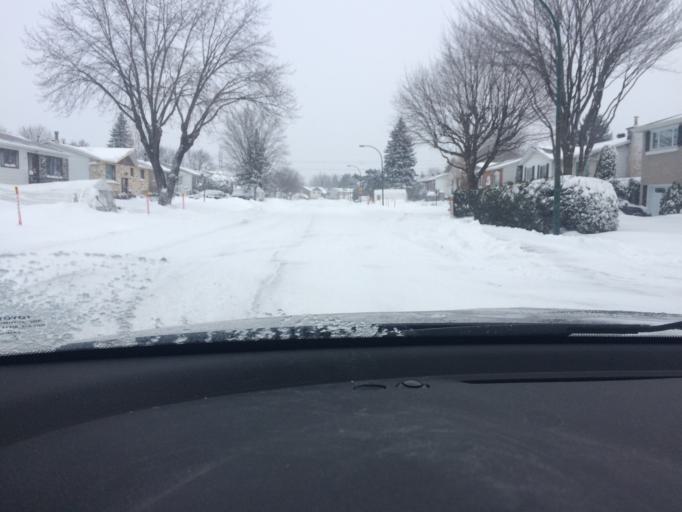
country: CA
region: Quebec
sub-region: Monteregie
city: Brossard
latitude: 45.4680
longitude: -73.4589
